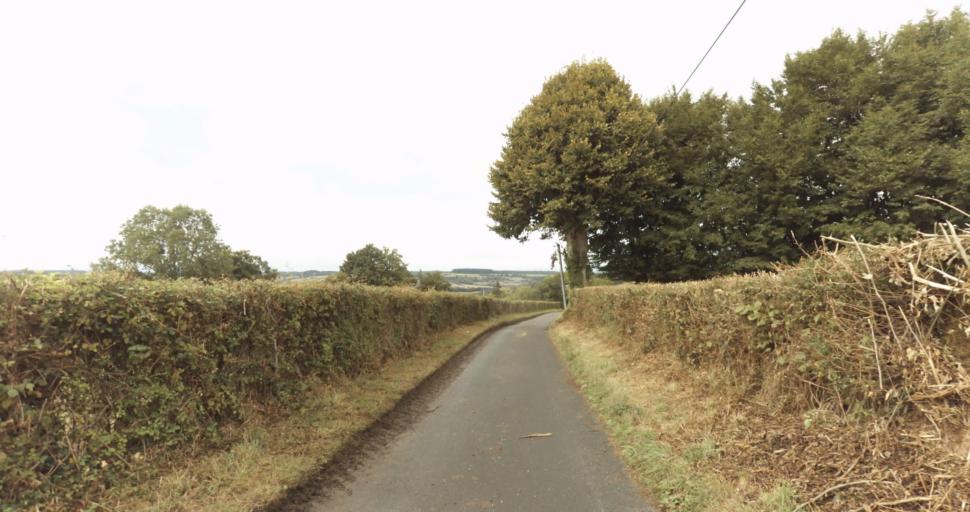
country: FR
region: Lower Normandy
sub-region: Departement de l'Orne
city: Vimoutiers
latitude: 48.8622
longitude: 0.1697
